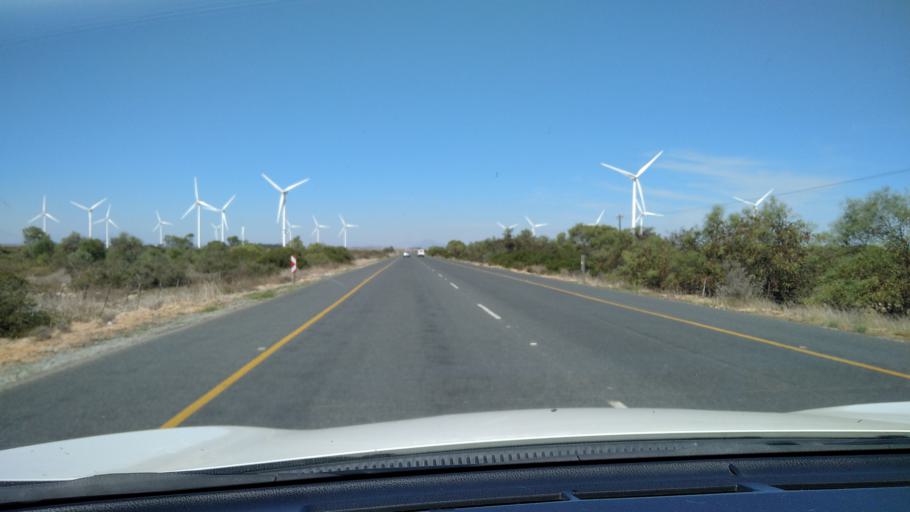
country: ZA
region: Western Cape
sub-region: West Coast District Municipality
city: Moorreesburg
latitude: -33.0784
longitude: 18.3850
